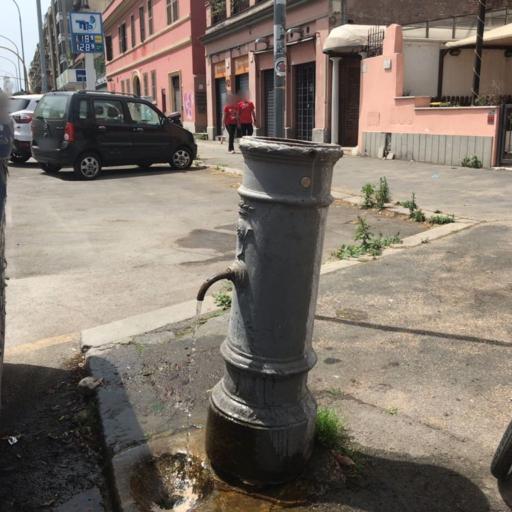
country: IT
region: Latium
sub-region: Citta metropolitana di Roma Capitale
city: Rome
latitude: 41.8659
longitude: 12.4791
